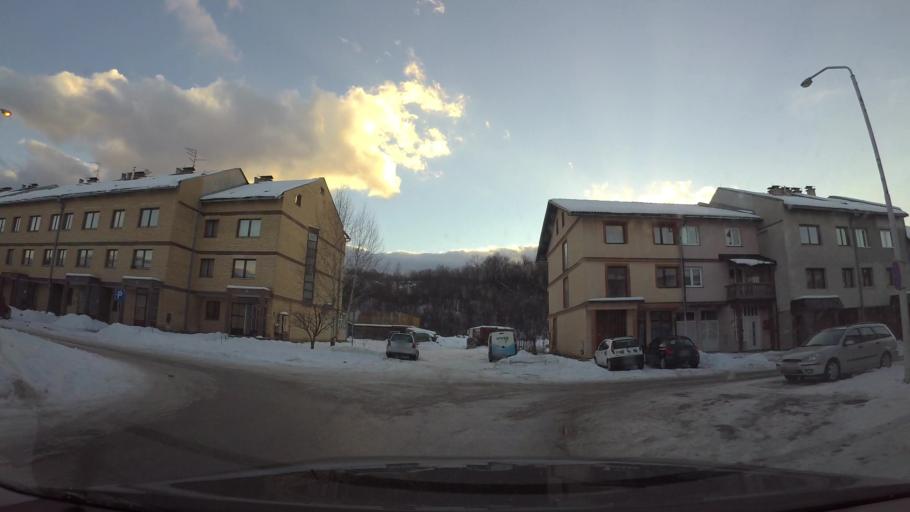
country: BA
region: Federation of Bosnia and Herzegovina
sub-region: Kanton Sarajevo
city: Sarajevo
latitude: 43.8100
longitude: 18.3615
